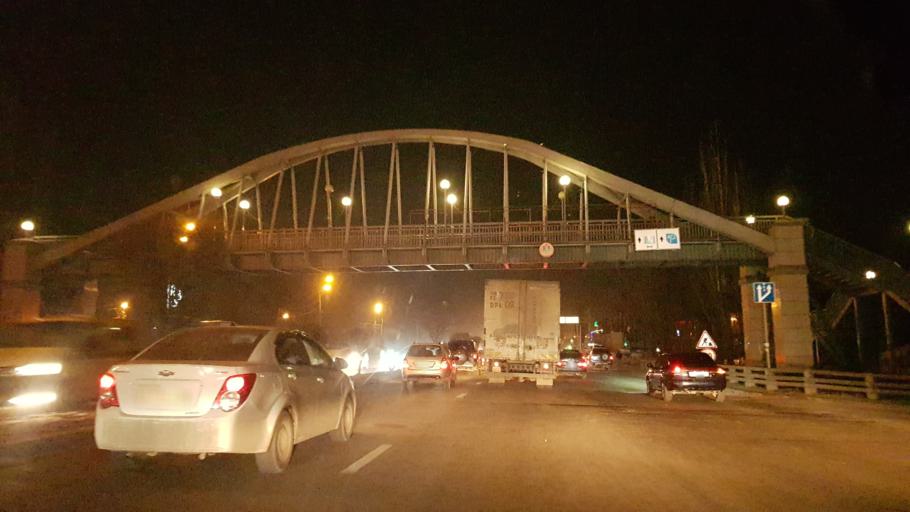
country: KZ
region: Almaty Qalasy
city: Almaty
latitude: 43.2634
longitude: 76.8607
